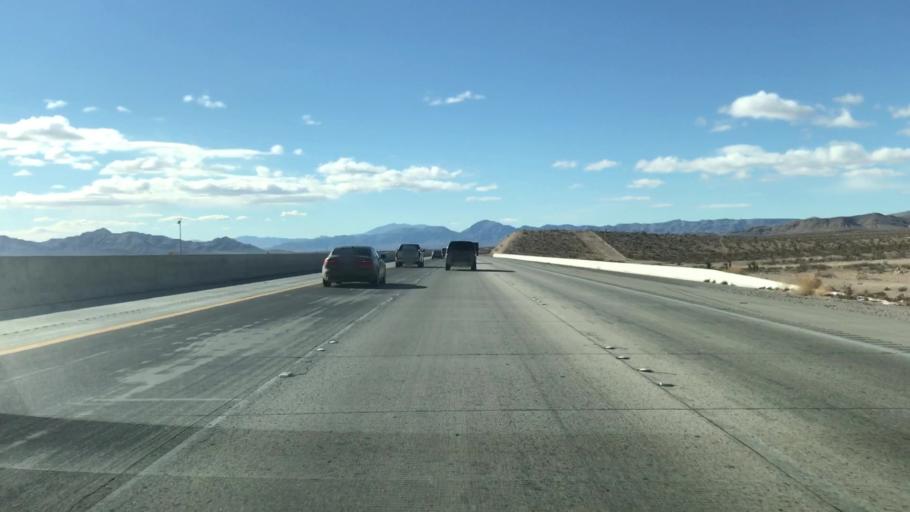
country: US
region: Nevada
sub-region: Clark County
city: Enterprise
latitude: 35.8692
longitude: -115.2453
